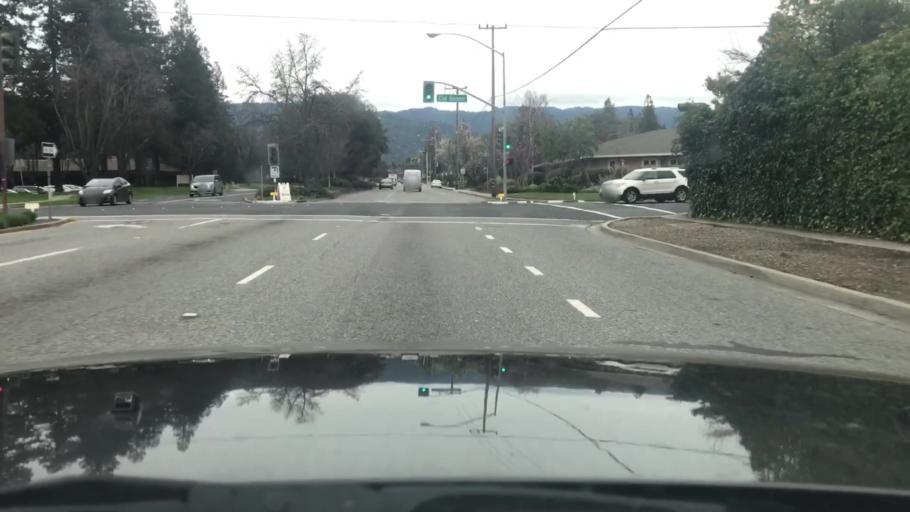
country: US
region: California
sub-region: Santa Clara County
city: Saratoga
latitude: 37.2816
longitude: -122.0027
